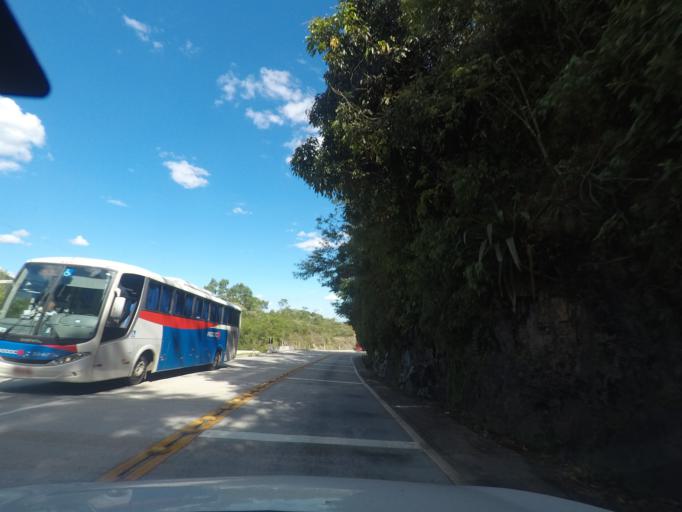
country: BR
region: Rio de Janeiro
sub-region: Guapimirim
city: Guapimirim
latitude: -22.4835
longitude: -42.9965
